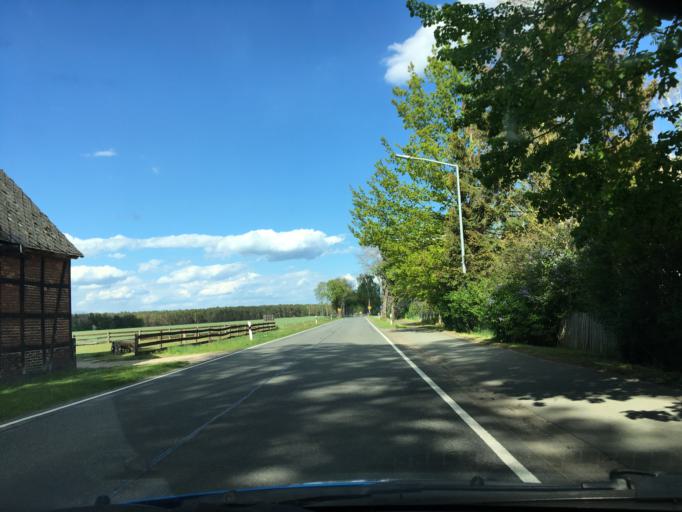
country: DE
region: Lower Saxony
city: Trebel
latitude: 52.9847
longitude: 11.2974
